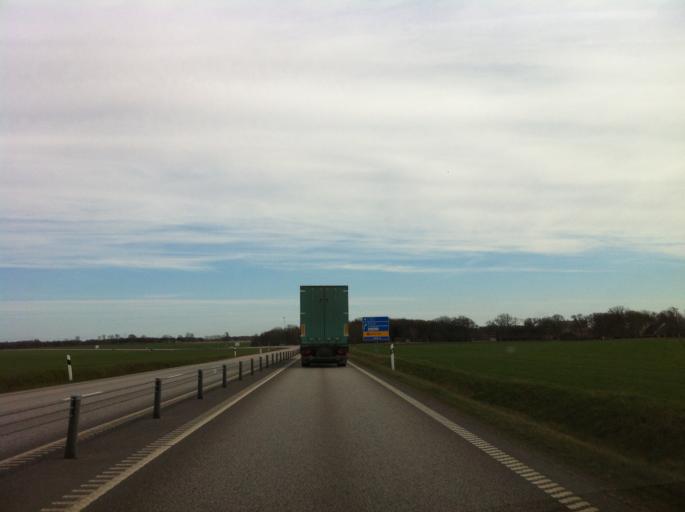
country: DK
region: Capital Region
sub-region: Helsingor Kommune
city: Helsingor
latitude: 56.1153
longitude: 12.6321
